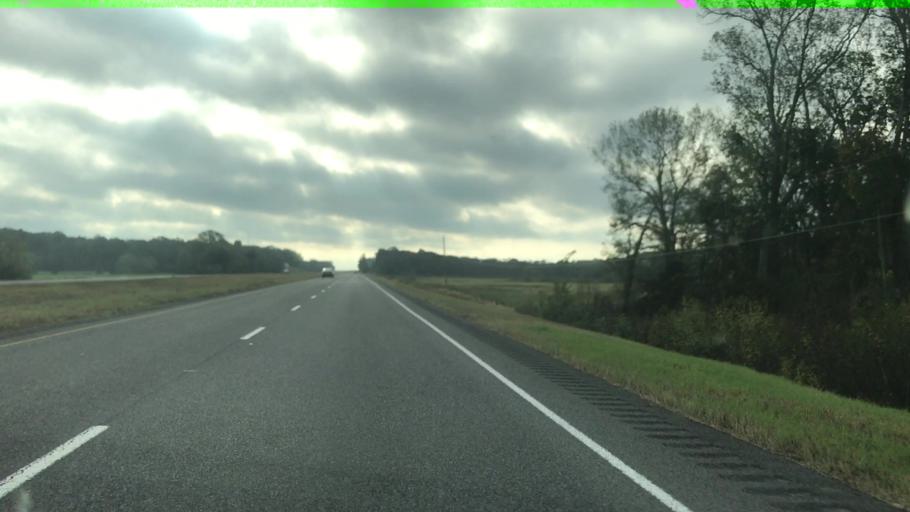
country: US
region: Alabama
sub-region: Morgan County
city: Danville
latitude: 34.4074
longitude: -87.1446
